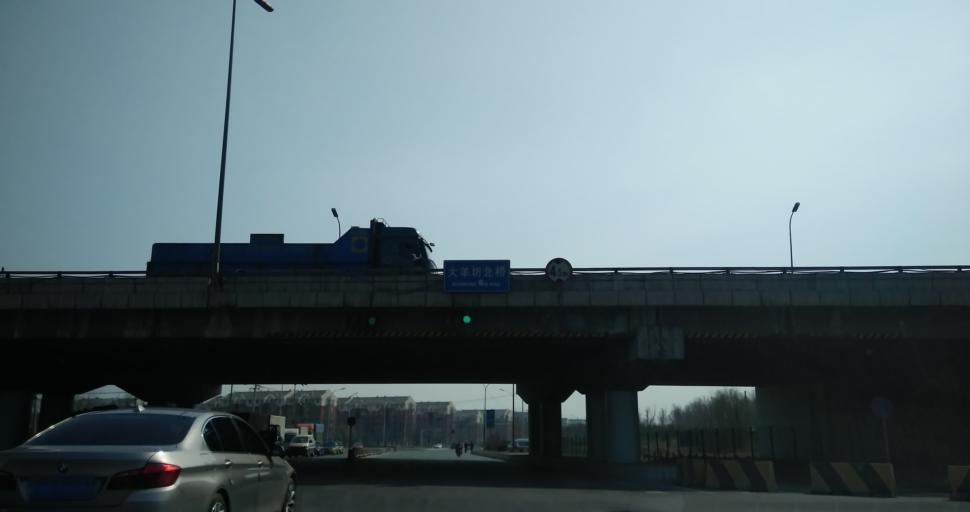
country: CN
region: Beijing
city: Jiugong
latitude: 39.8215
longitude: 116.5057
